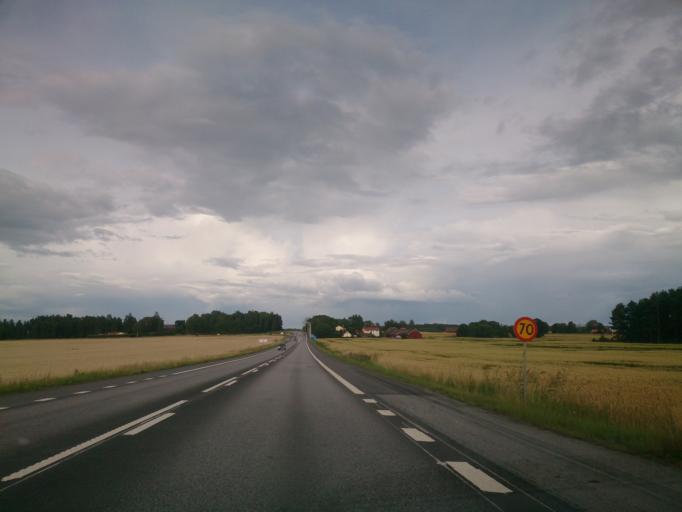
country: SE
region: OEstergoetland
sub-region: Linkopings Kommun
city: Linghem
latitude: 58.4289
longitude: 15.7099
